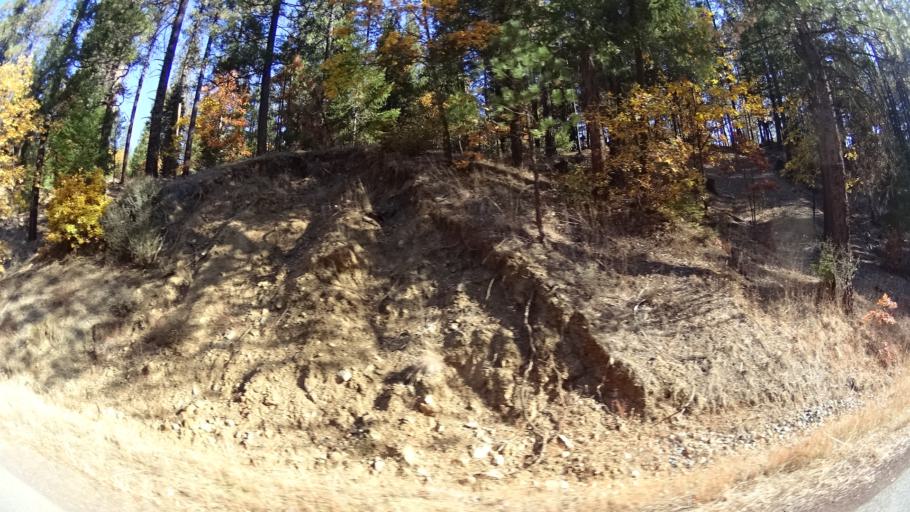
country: US
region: California
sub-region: Siskiyou County
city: Happy Camp
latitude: 41.6403
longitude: -123.0214
